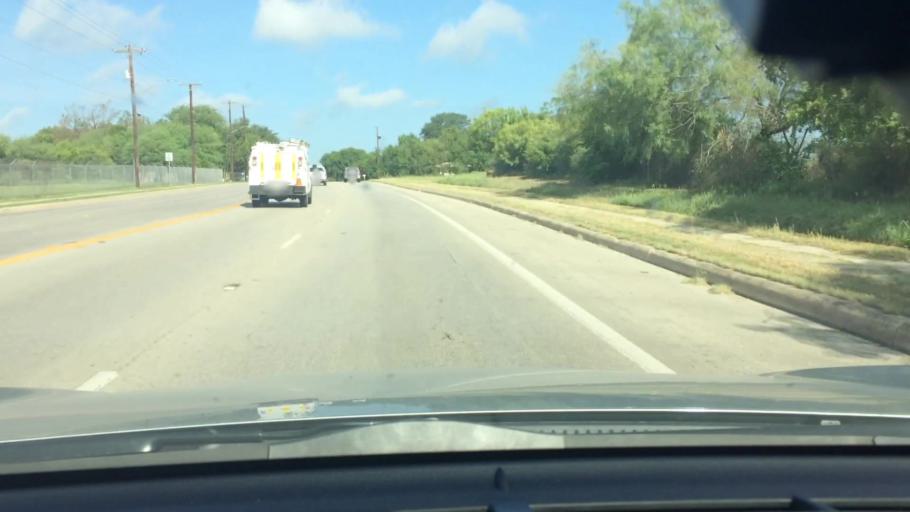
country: US
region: Texas
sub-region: Bexar County
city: China Grove
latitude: 29.3735
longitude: -98.3973
